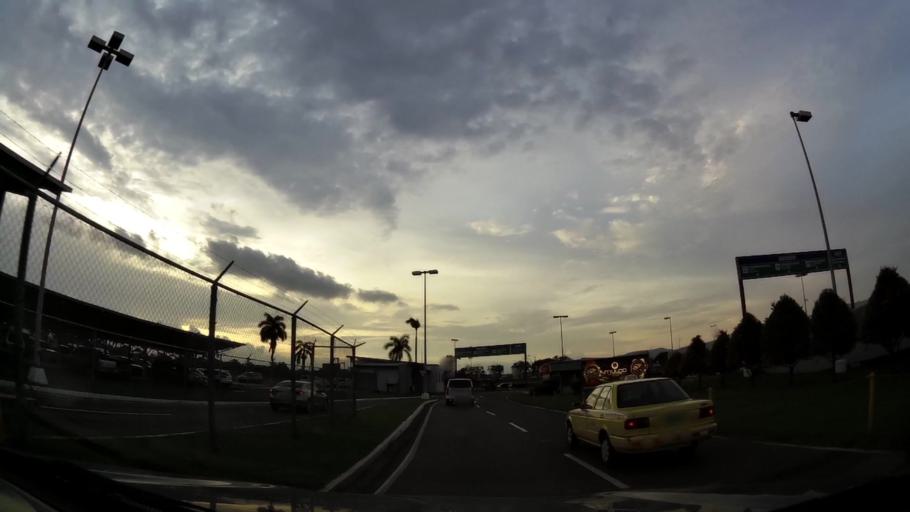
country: PA
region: Panama
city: Tocumen
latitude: 9.0685
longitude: -79.3877
